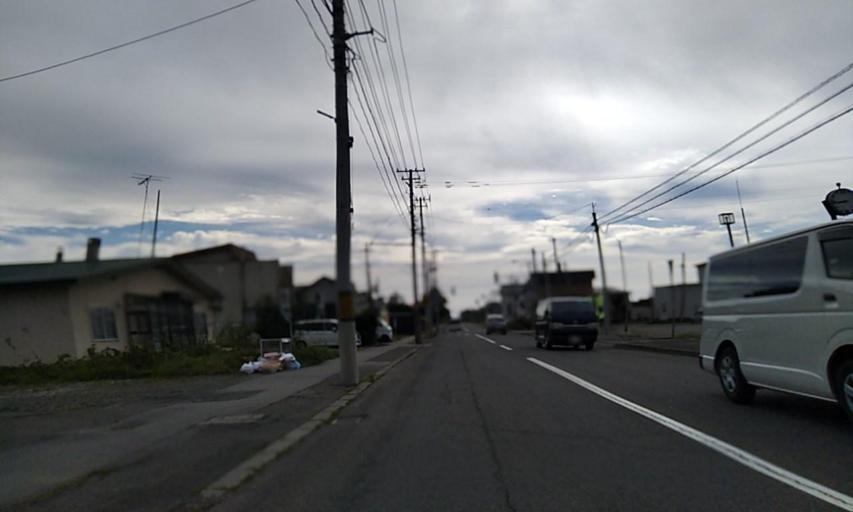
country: JP
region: Hokkaido
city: Obihiro
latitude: 42.8492
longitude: 143.1664
